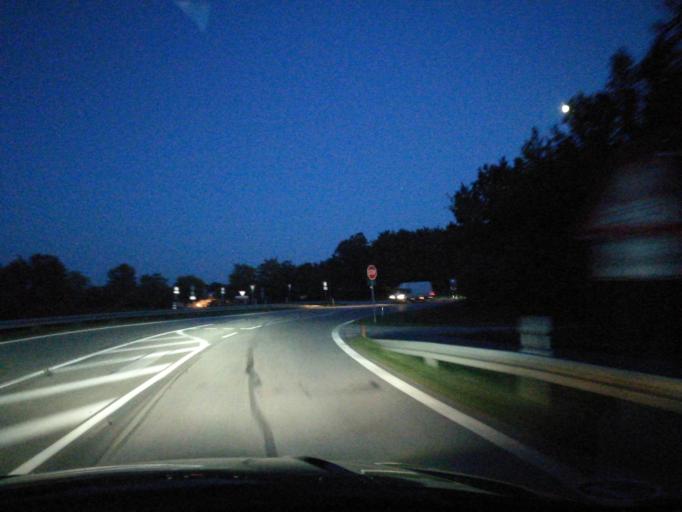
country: DE
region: Bavaria
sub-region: Upper Palatinate
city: Pentling
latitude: 48.9780
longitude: 12.0664
